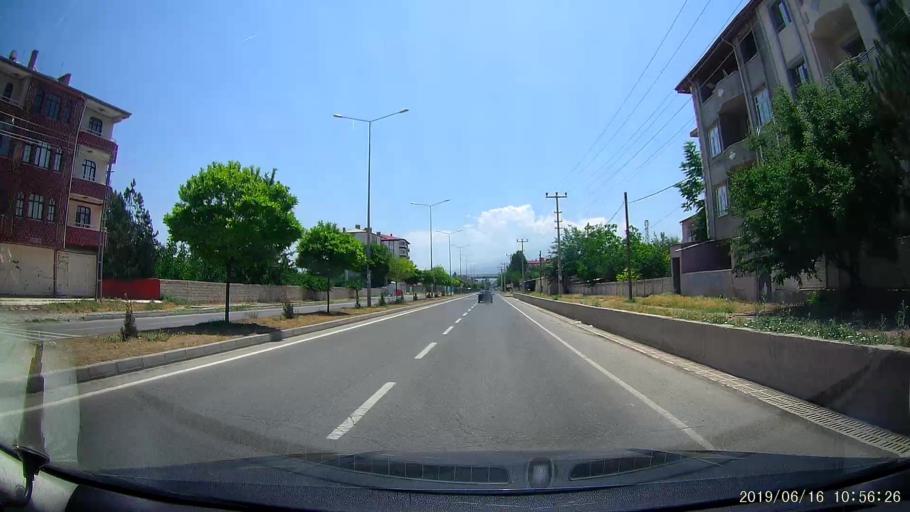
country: TR
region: Igdir
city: Igdir
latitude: 39.9298
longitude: 44.0223
